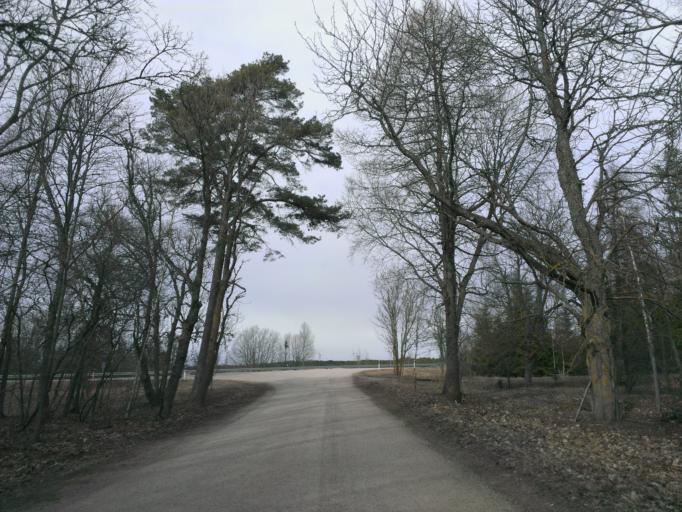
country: EE
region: Laeaene
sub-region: Lihula vald
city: Lihula
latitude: 58.5895
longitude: 23.5374
